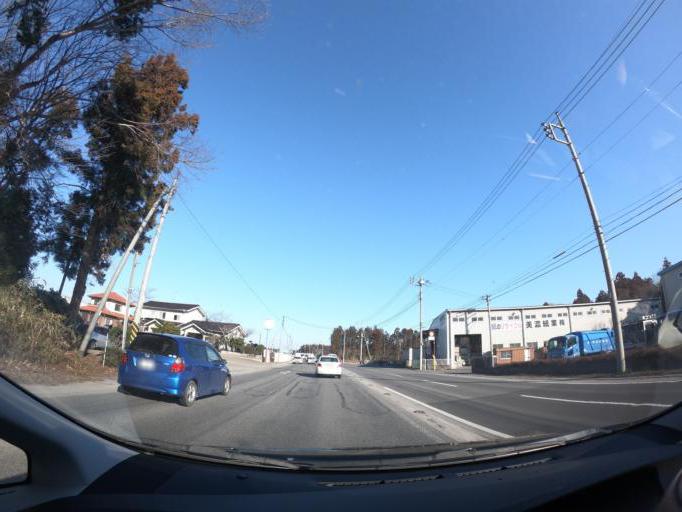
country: JP
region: Ibaraki
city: Ishige
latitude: 36.0881
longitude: 140.0386
